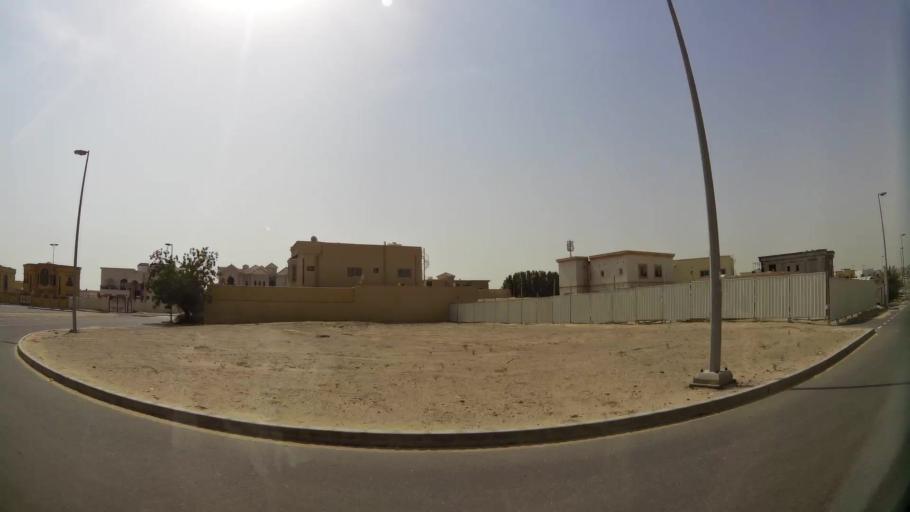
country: AE
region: Ash Shariqah
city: Sharjah
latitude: 25.2575
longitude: 55.4691
